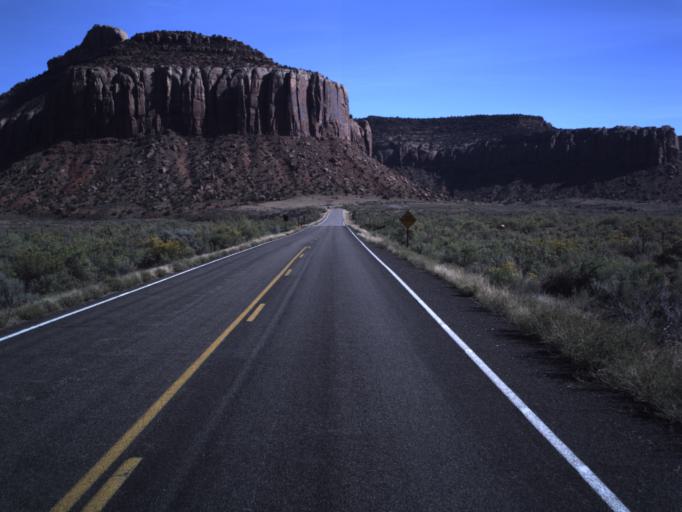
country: US
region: Utah
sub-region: San Juan County
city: Monticello
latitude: 38.0704
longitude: -109.5573
